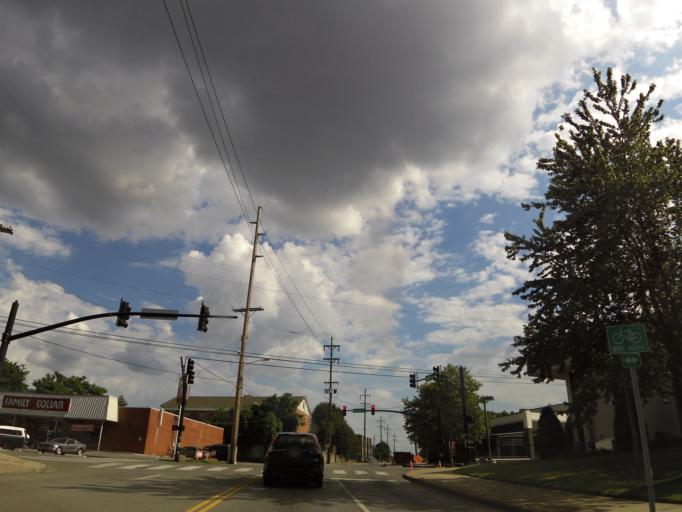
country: US
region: Tennessee
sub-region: Davidson County
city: Nashville
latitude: 36.1773
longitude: -86.7515
